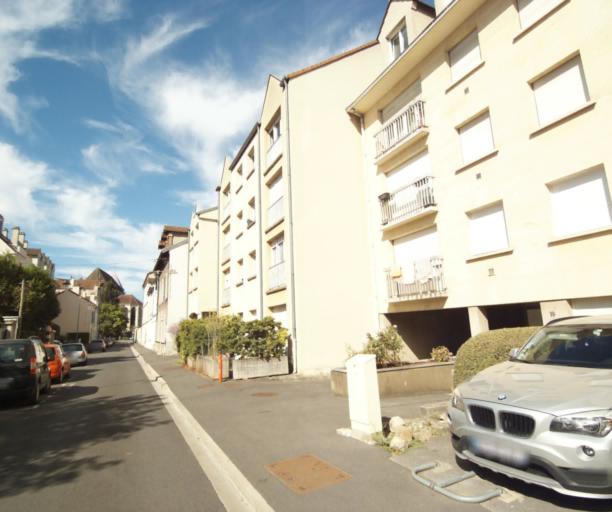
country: FR
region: Ile-de-France
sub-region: Departement de Seine-et-Marne
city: Thorigny-sur-Marne
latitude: 48.8783
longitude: 2.7086
